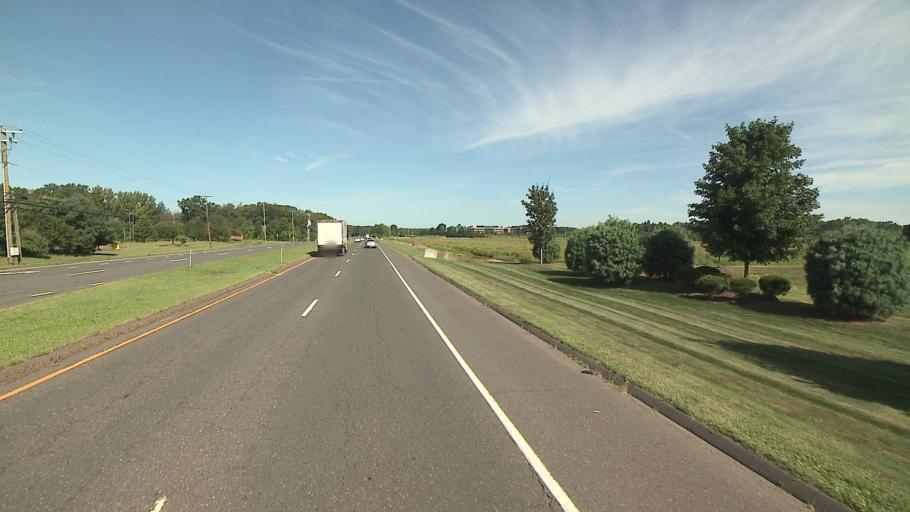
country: US
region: Connecticut
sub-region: Hartford County
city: Tariffville
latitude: 41.8718
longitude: -72.7250
